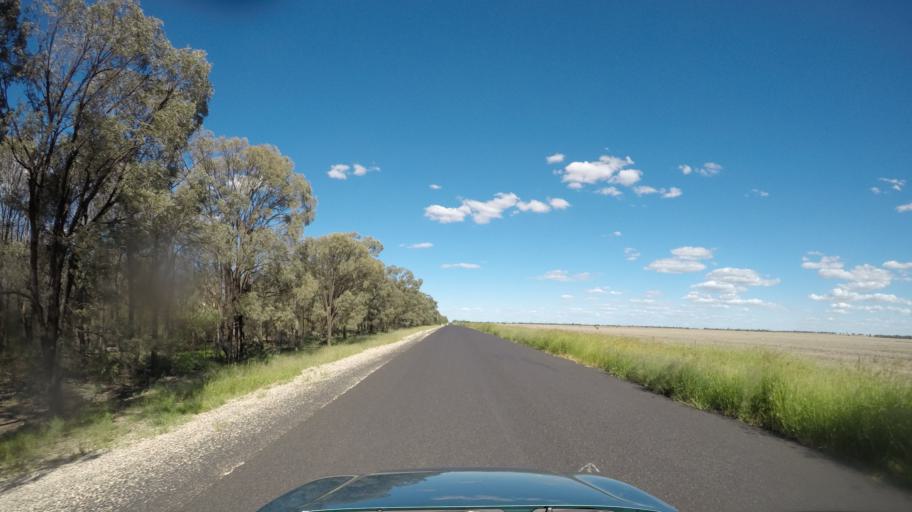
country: AU
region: Queensland
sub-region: Goondiwindi
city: Goondiwindi
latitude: -28.1591
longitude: 150.3962
